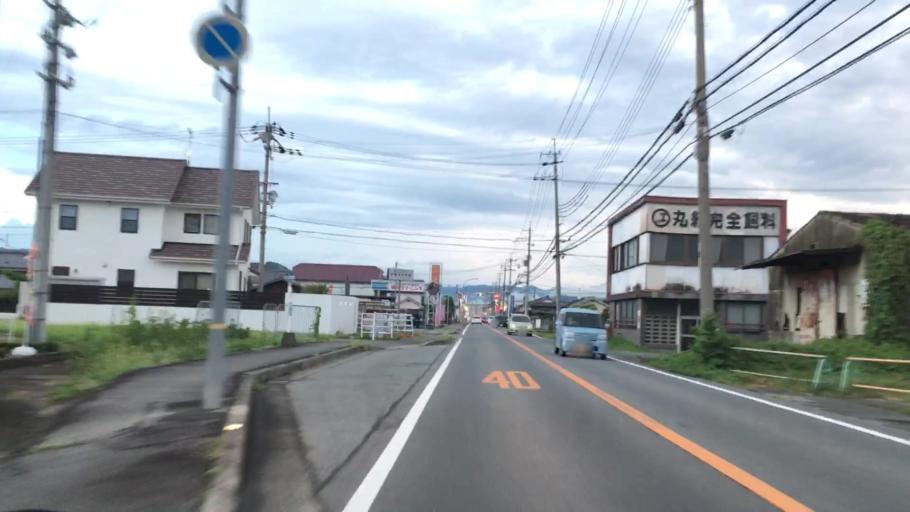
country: JP
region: Hyogo
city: Himeji
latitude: 34.9179
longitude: 134.7416
